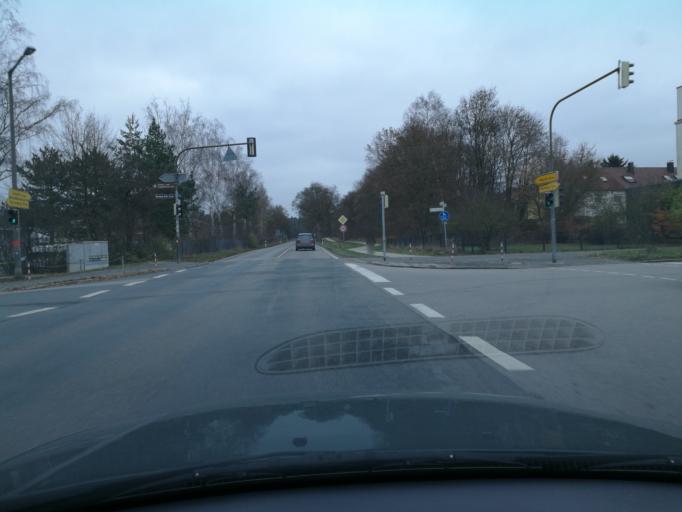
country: DE
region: Bavaria
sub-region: Regierungsbezirk Mittelfranken
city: Feucht
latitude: 49.3994
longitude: 11.1759
